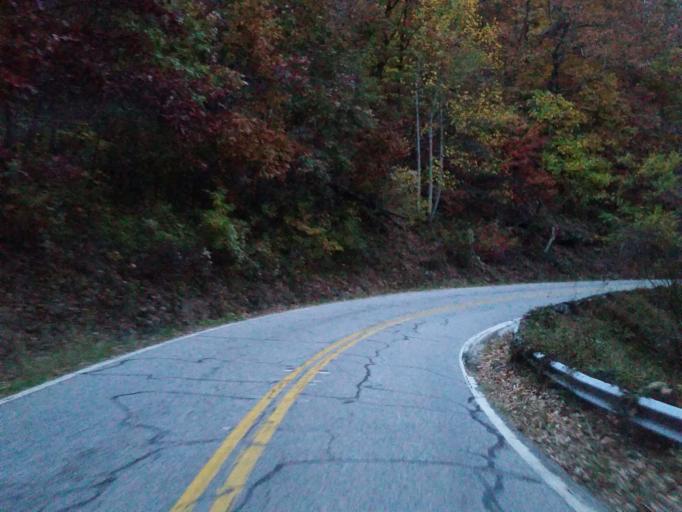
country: US
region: Georgia
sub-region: Lumpkin County
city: Dahlonega
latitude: 34.6750
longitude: -83.9933
